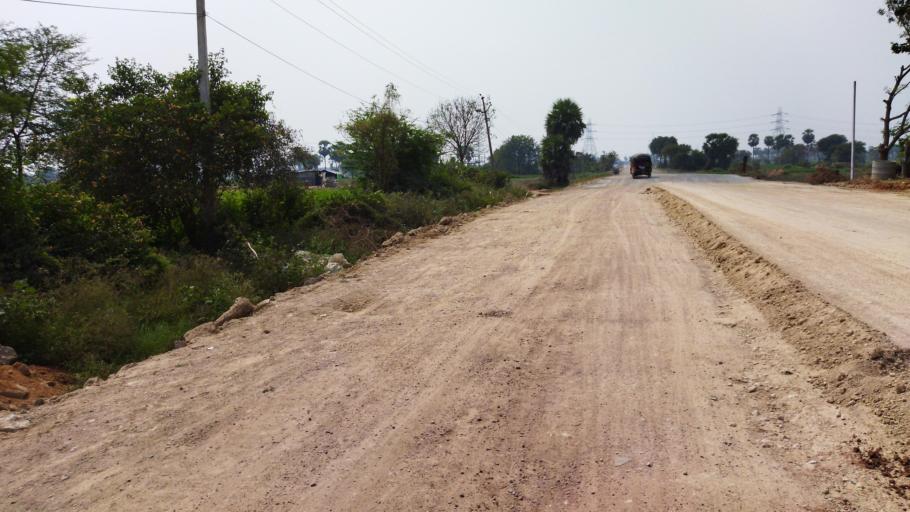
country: IN
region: Telangana
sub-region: Nalgonda
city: Nalgonda
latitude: 17.1343
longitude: 79.3799
